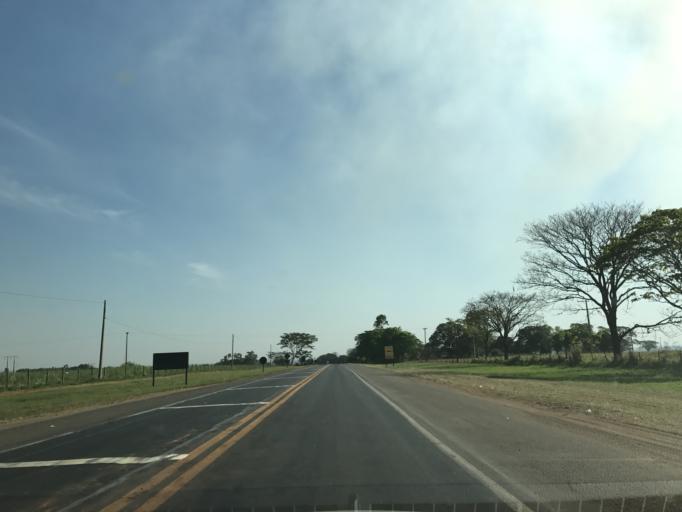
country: BR
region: Sao Paulo
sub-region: Penapolis
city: Penapolis
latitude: -21.3969
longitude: -50.1076
